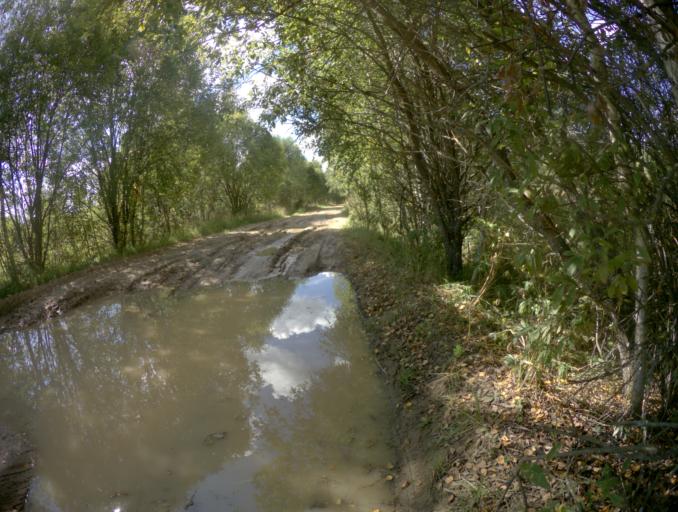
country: RU
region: Vladimir
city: Nikologory
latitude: 56.0274
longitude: 41.9450
